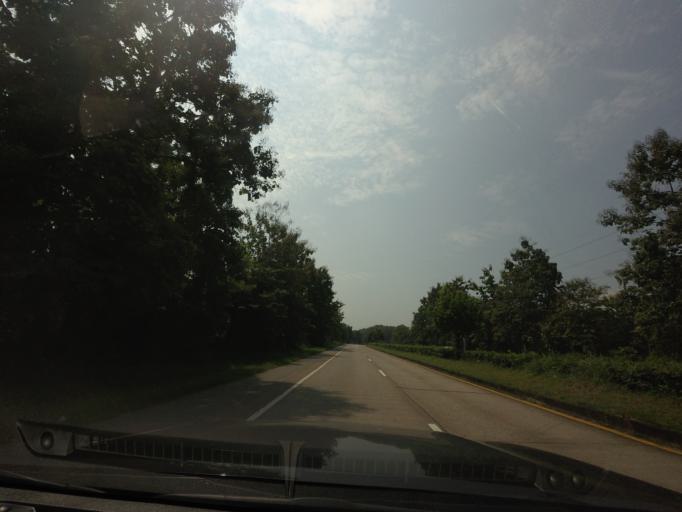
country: TH
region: Phrae
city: Sung Men
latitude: 18.0016
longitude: 100.1035
